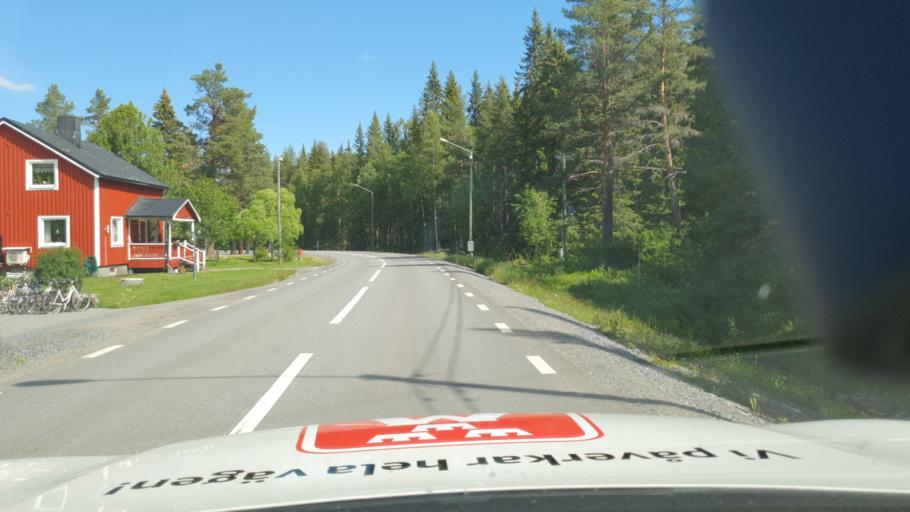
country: SE
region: Vaesterbotten
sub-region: Skelleftea Kommun
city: Langsele
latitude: 64.7780
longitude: 20.3369
